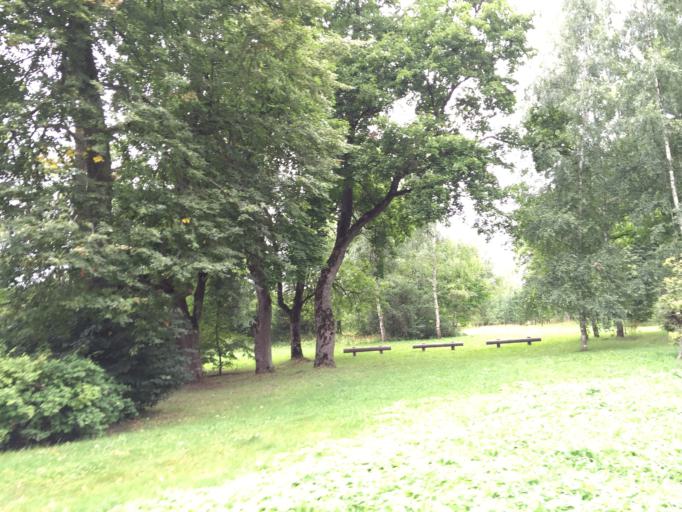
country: LV
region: Dobeles Rajons
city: Dobele
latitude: 56.7136
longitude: 23.1860
